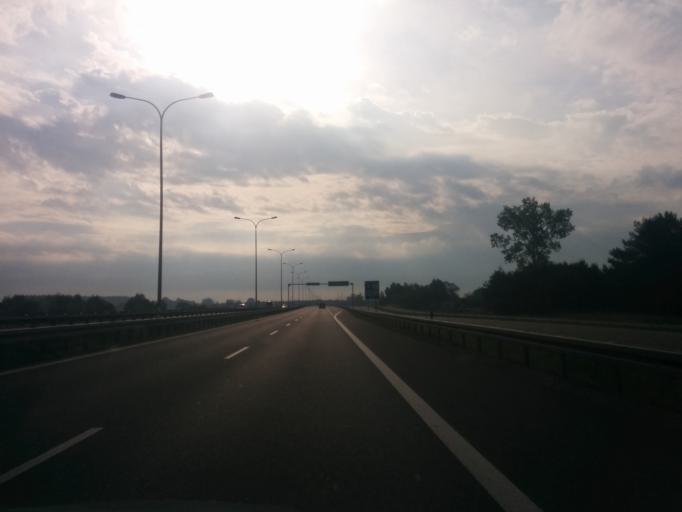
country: PL
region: Masovian Voivodeship
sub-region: Powiat bialobrzeski
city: Stara Blotnica
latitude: 51.5745
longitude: 21.0123
